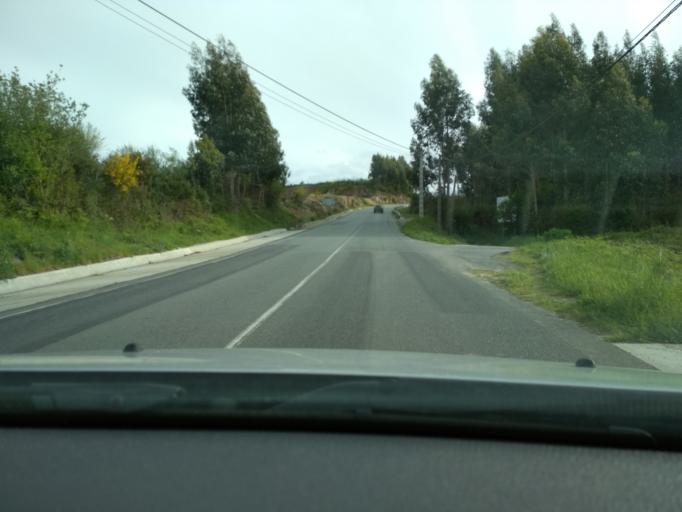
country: ES
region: Galicia
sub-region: Provincia da Coruna
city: Culleredo
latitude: 43.2848
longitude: -8.3923
